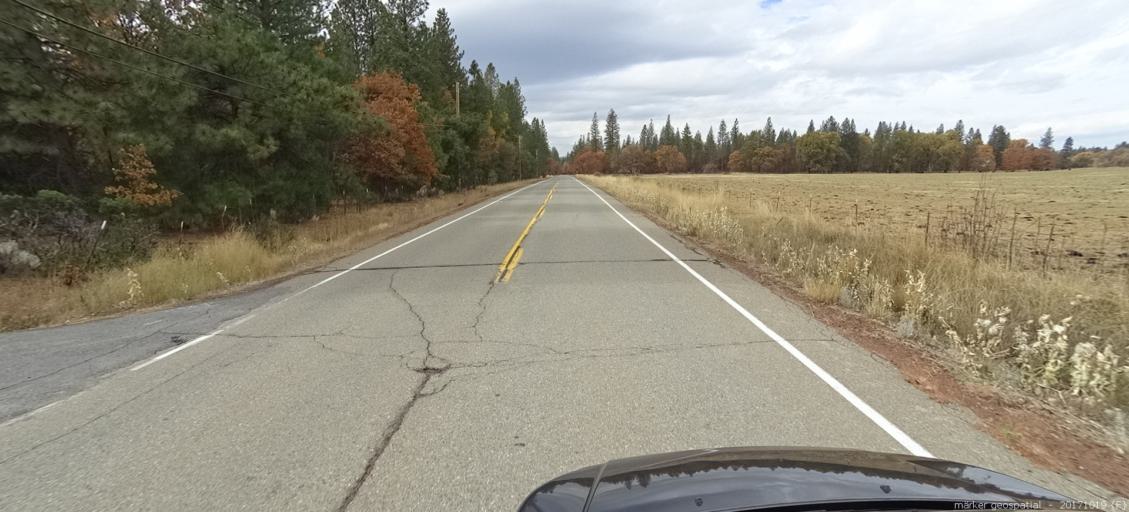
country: US
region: California
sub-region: Shasta County
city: Burney
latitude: 41.0944
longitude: -121.5202
